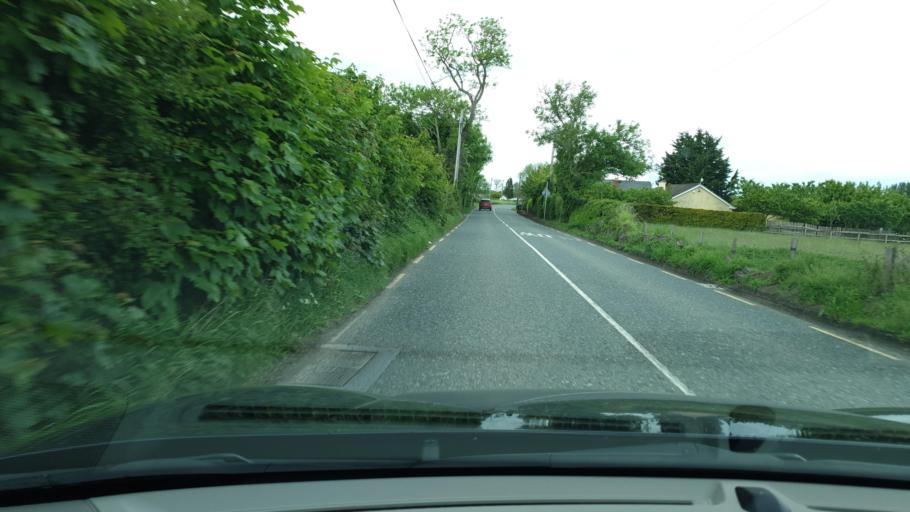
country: IE
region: Leinster
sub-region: An Mhi
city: Ratoath
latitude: 53.5295
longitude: -6.4504
